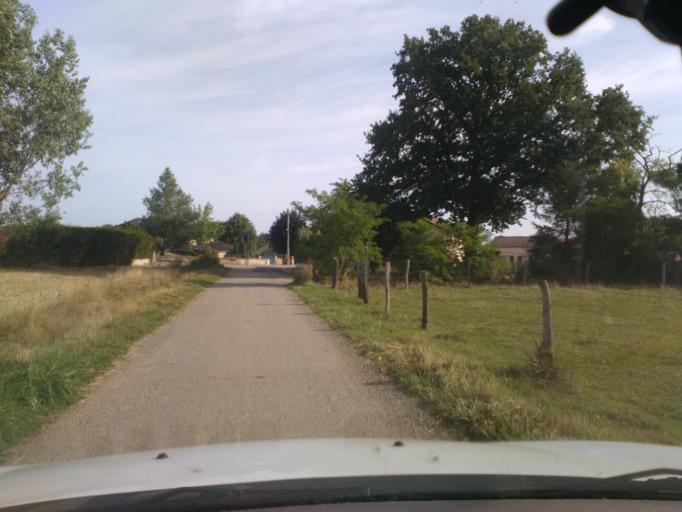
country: FR
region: Lorraine
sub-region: Departement des Vosges
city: Mirecourt
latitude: 48.3312
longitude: 6.0953
